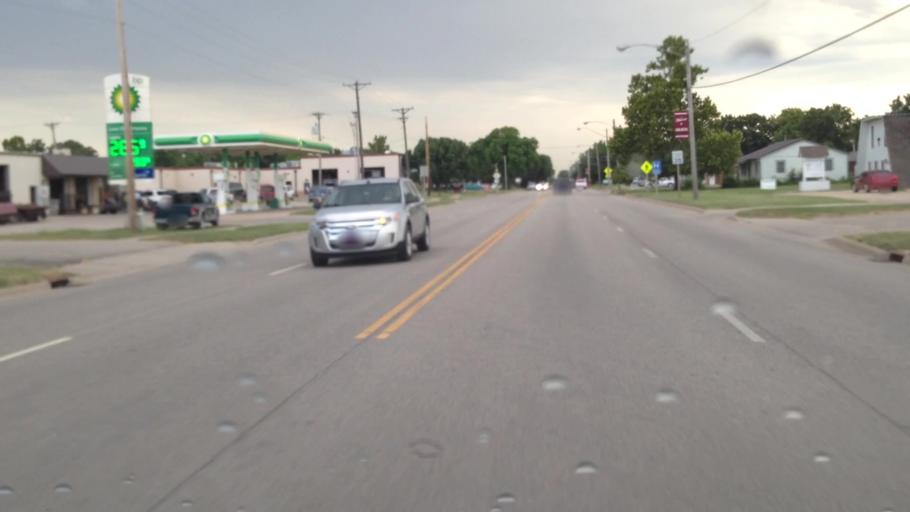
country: US
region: Kansas
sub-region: Coffey County
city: Burlington
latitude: 38.2041
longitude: -95.7386
